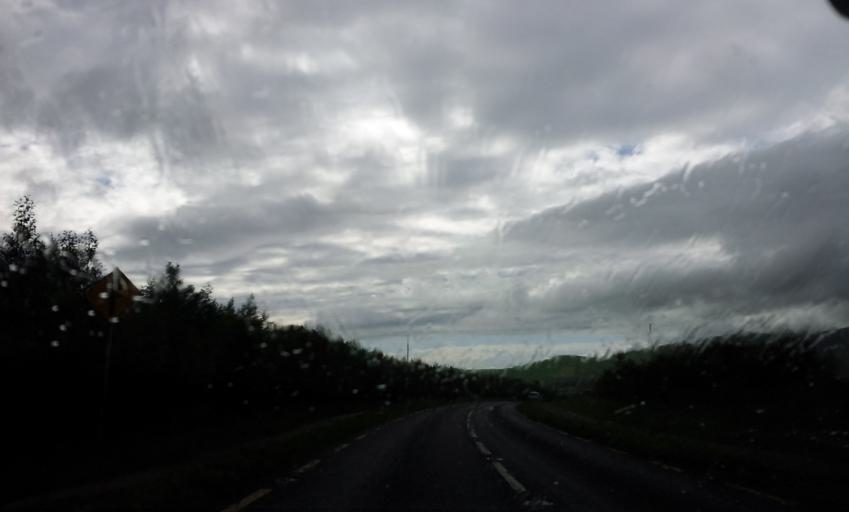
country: IE
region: Munster
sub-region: Ciarrai
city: Dingle
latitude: 52.1605
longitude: -10.0294
